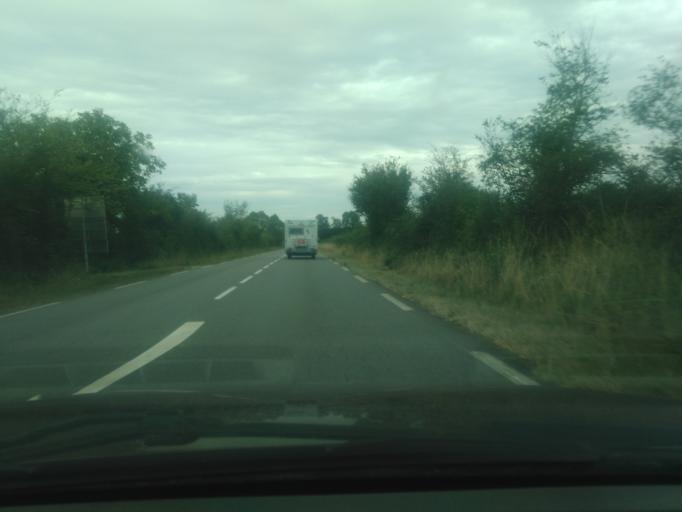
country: FR
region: Auvergne
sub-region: Departement de l'Allier
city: Ainay-le-Chateau
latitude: 46.7506
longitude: 2.7764
